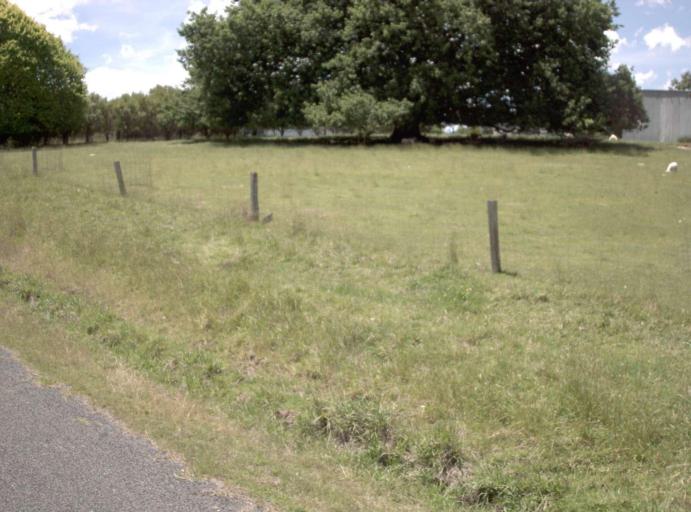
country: AU
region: New South Wales
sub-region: Bombala
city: Bombala
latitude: -37.4110
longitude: 149.0095
